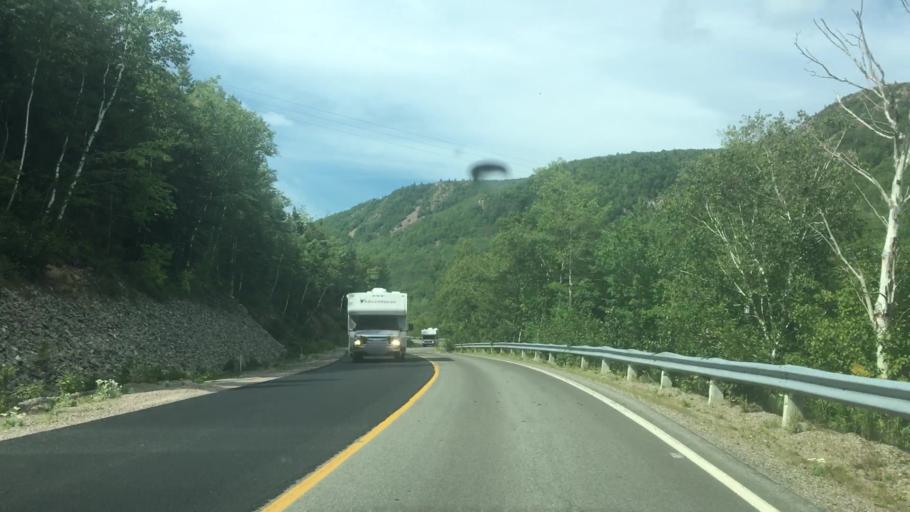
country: CA
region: Nova Scotia
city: Sydney Mines
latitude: 46.5799
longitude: -60.3903
